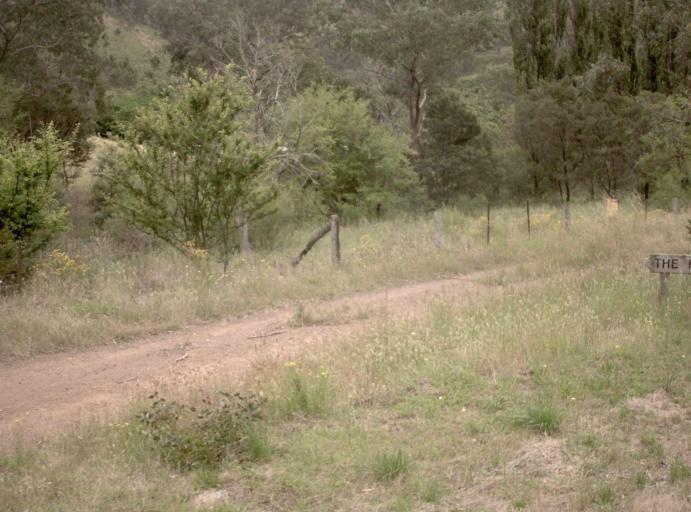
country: AU
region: Victoria
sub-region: East Gippsland
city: Bairnsdale
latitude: -37.5351
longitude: 147.2129
